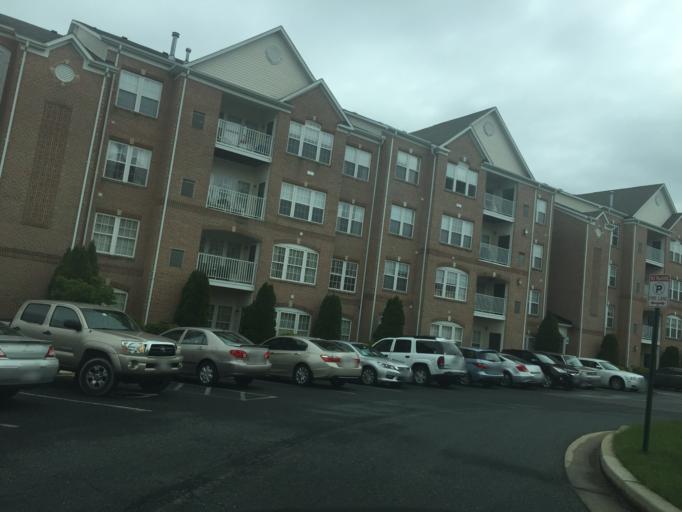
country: US
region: Maryland
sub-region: Baltimore County
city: Perry Hall
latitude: 39.4080
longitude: -76.4458
